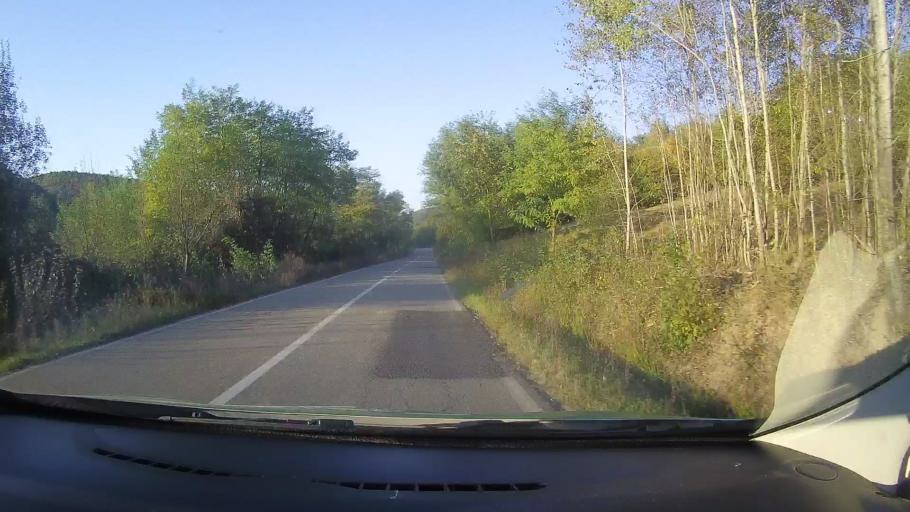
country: RO
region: Timis
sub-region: Comuna Fardea
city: Fardea
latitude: 45.6986
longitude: 22.1603
